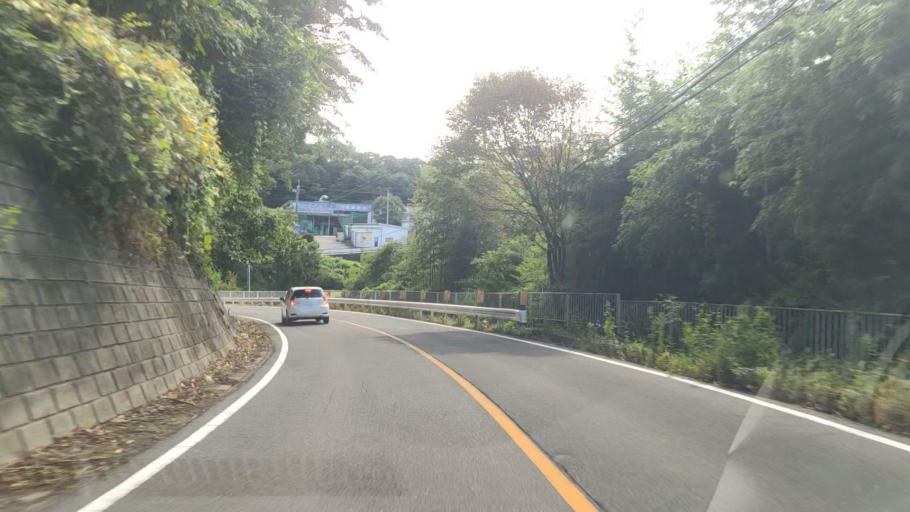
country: JP
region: Gunma
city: Numata
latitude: 36.6243
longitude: 139.0226
